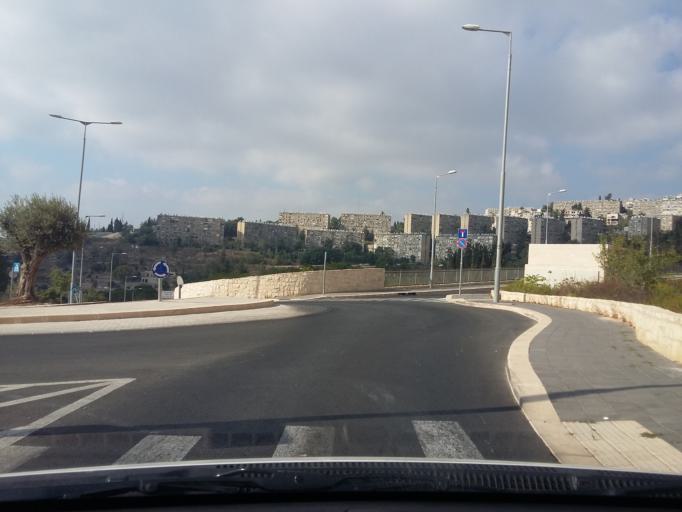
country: PS
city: Khallat Hamamah
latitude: 31.7629
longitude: 35.1693
